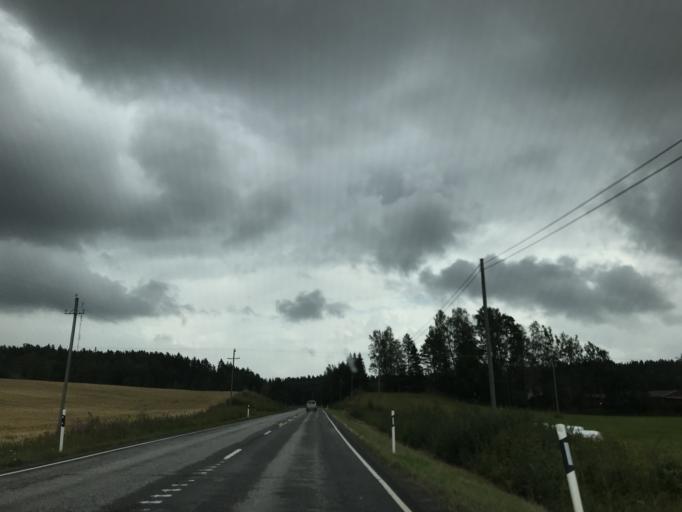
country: FI
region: Varsinais-Suomi
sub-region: Salo
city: Pernioe
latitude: 60.0885
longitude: 23.2282
